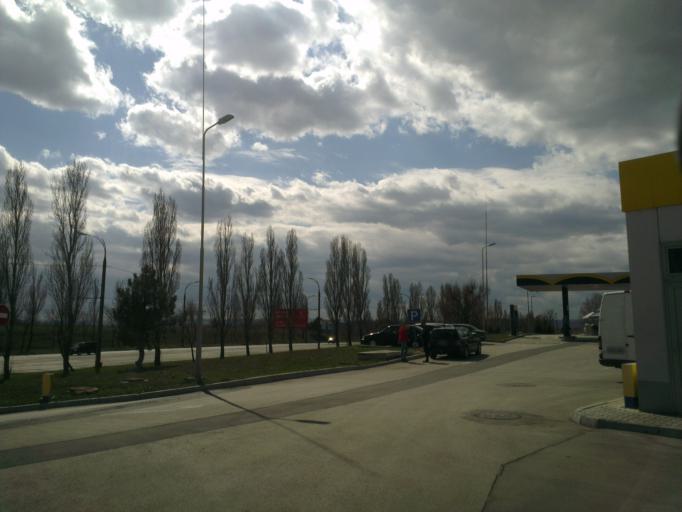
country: MD
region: Laloveni
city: Ialoveni
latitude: 46.9941
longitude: 28.7940
